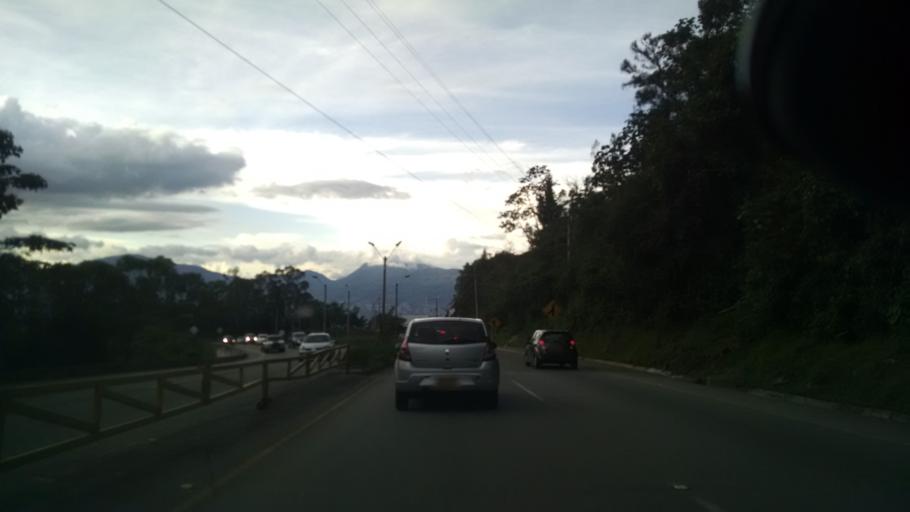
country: CO
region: Antioquia
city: Envigado
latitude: 6.1701
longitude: -75.5457
